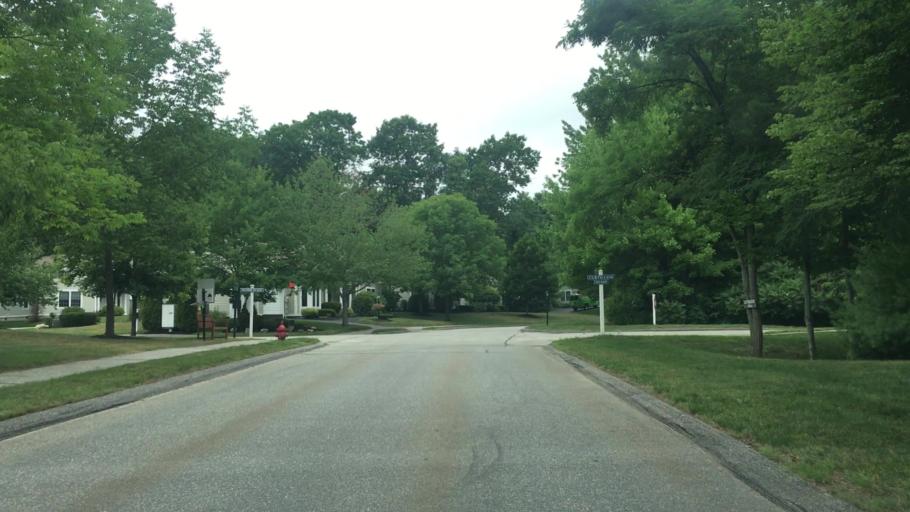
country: US
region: Maine
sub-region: Sagadahoc County
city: Topsham
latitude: 43.9335
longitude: -69.9589
